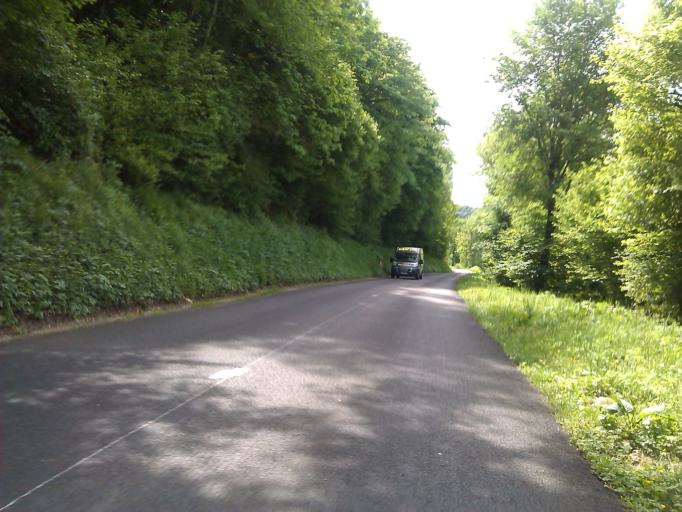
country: FR
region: Franche-Comte
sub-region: Departement du Doubs
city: Boussieres
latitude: 47.1625
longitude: 5.8960
